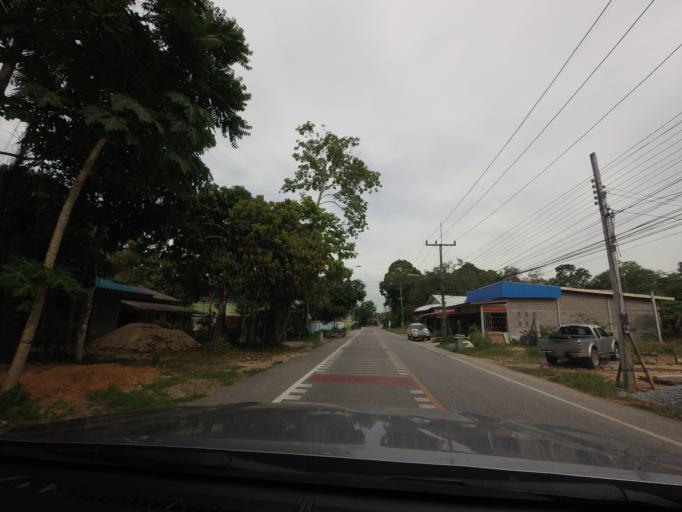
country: TH
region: Yala
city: Raman
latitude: 6.4580
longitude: 101.4434
